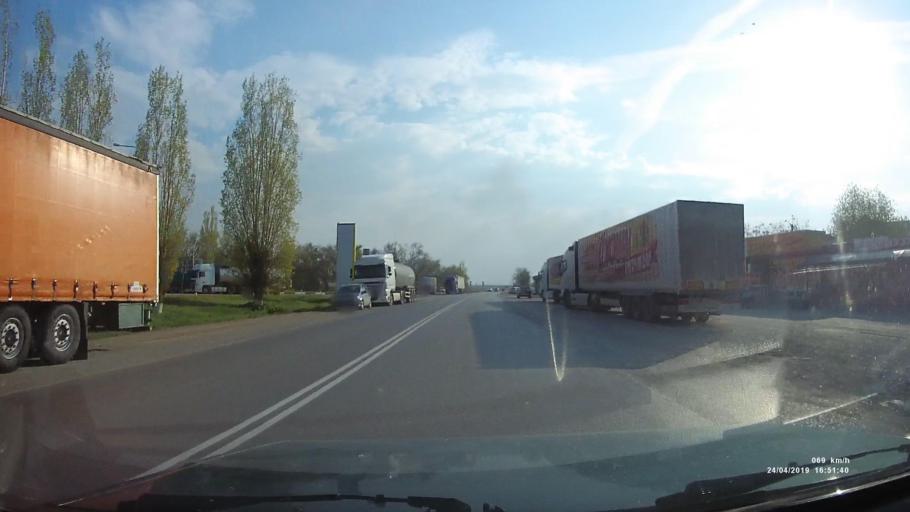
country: RU
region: Rostov
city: Proletarsk
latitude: 46.6949
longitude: 41.7446
